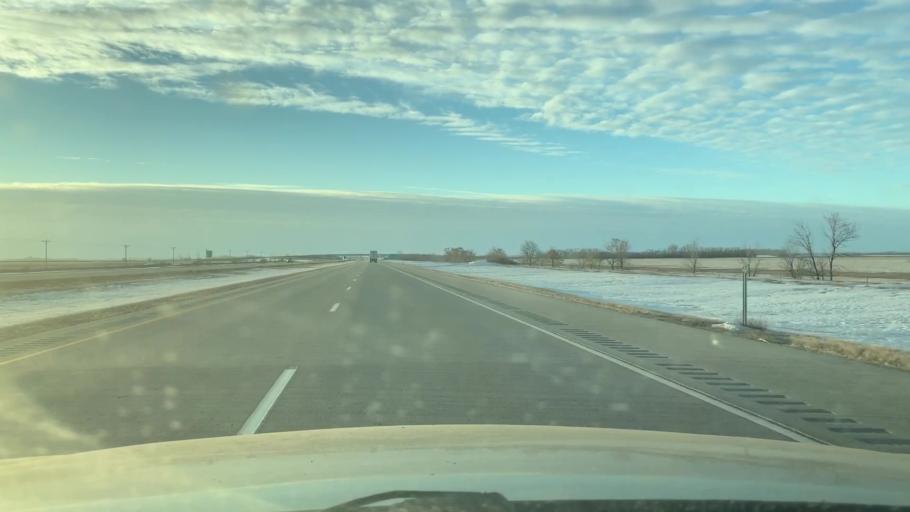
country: US
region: North Dakota
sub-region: Cass County
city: Casselton
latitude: 46.8758
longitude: -97.3302
